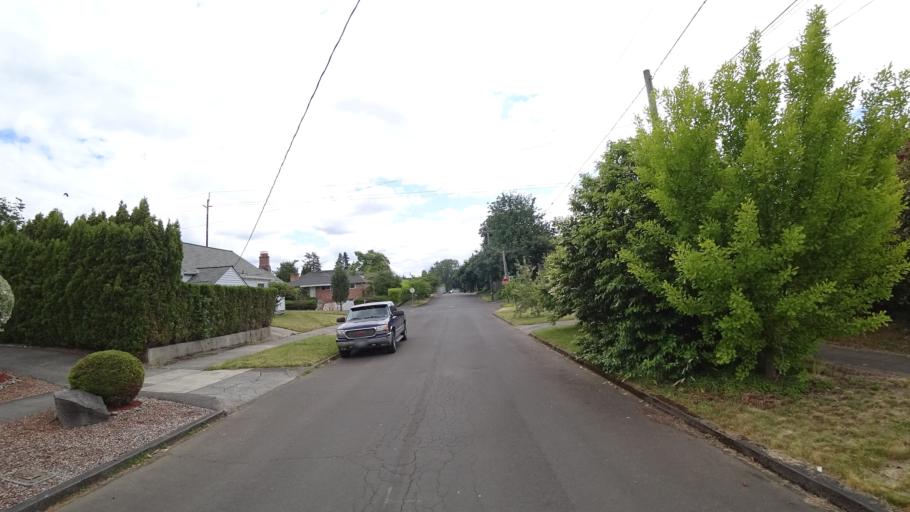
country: US
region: Oregon
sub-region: Washington County
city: West Haven
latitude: 45.5821
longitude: -122.7305
